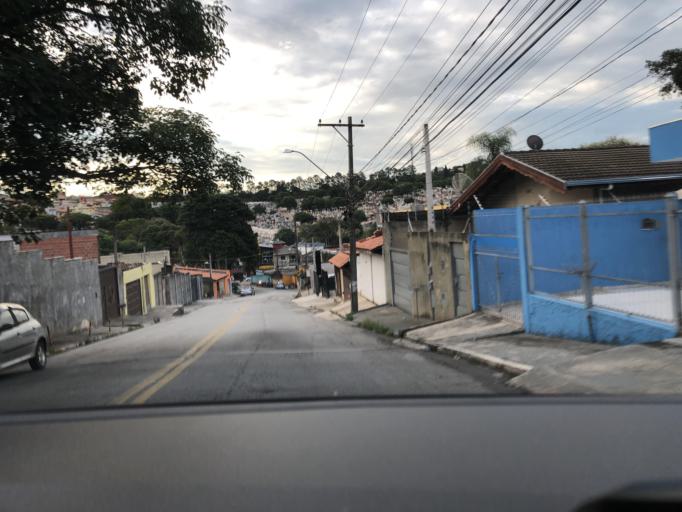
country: BR
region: Sao Paulo
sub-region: Varzea Paulista
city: Varzea Paulista
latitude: -23.2180
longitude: -46.8538
